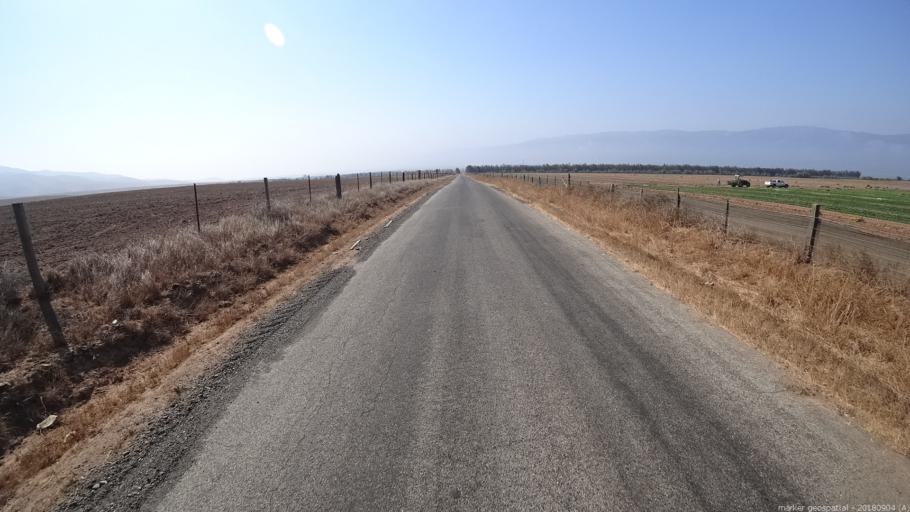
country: US
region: California
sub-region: Monterey County
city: Gonzales
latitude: 36.5029
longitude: -121.3648
